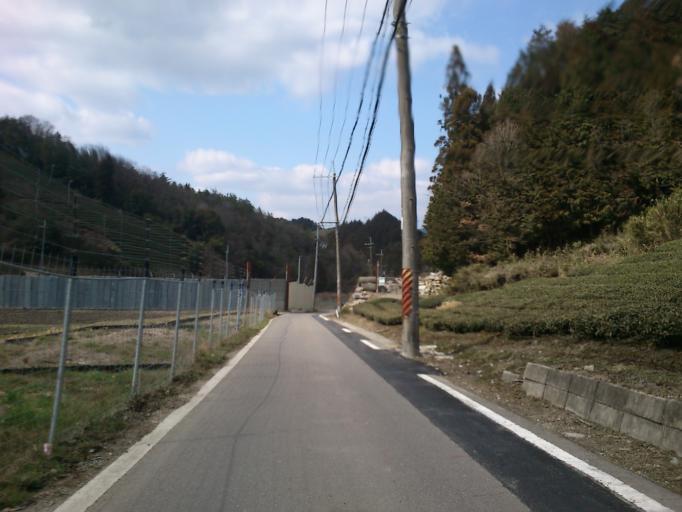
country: JP
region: Nara
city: Nara-shi
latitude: 34.7772
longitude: 135.9081
